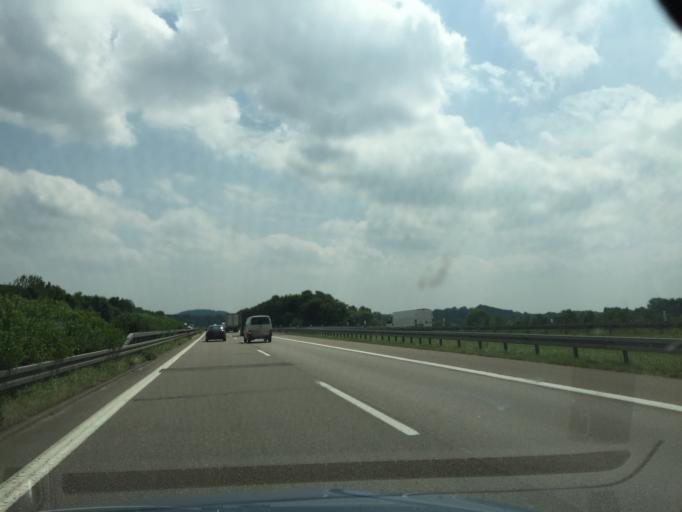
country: DE
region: Bavaria
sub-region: Swabia
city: Holzheim
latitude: 48.4145
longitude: 10.0940
